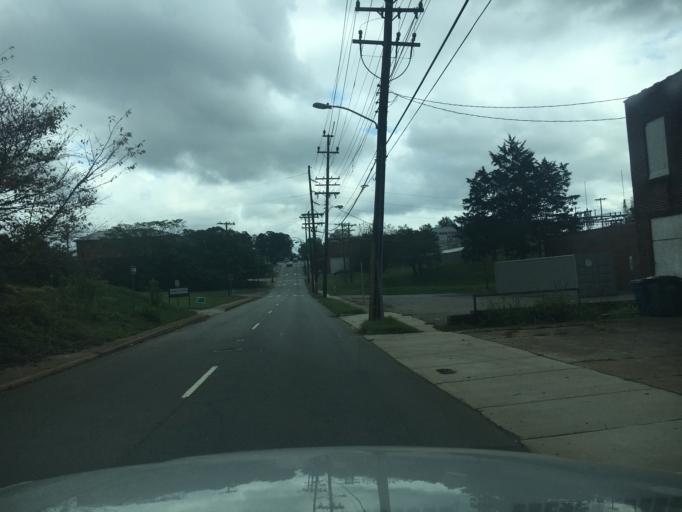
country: US
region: North Carolina
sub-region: Catawba County
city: Hickory
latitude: 35.7299
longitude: -81.3407
